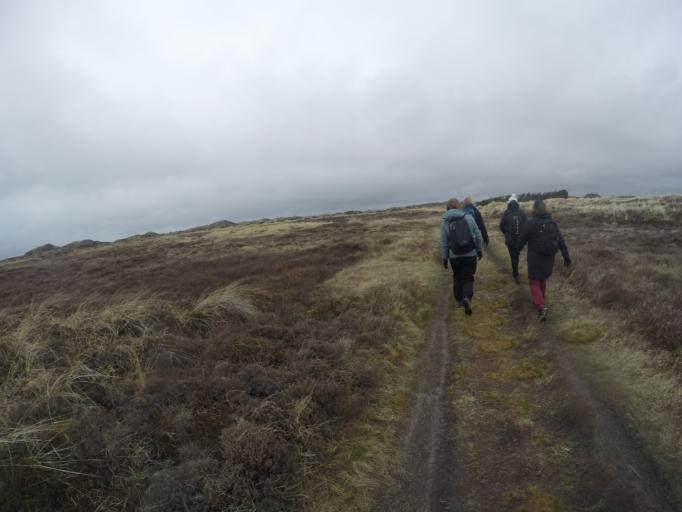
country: DK
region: North Denmark
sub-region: Thisted Kommune
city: Hurup
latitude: 56.8604
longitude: 8.2908
